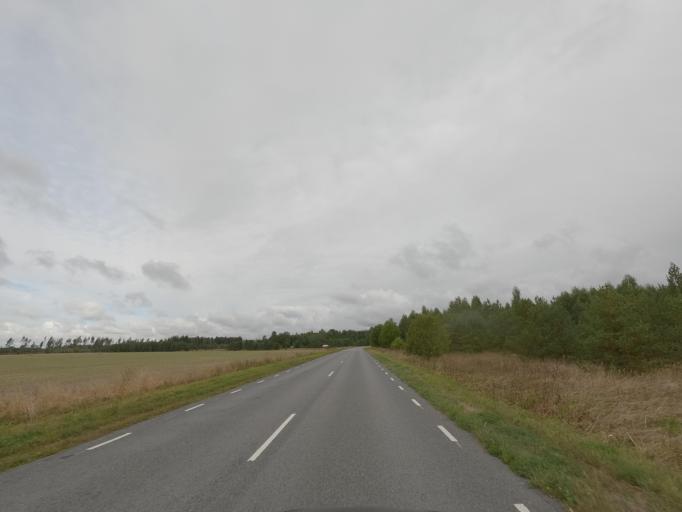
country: EE
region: Raplamaa
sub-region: Maerjamaa vald
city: Marjamaa
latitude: 59.0186
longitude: 24.5616
